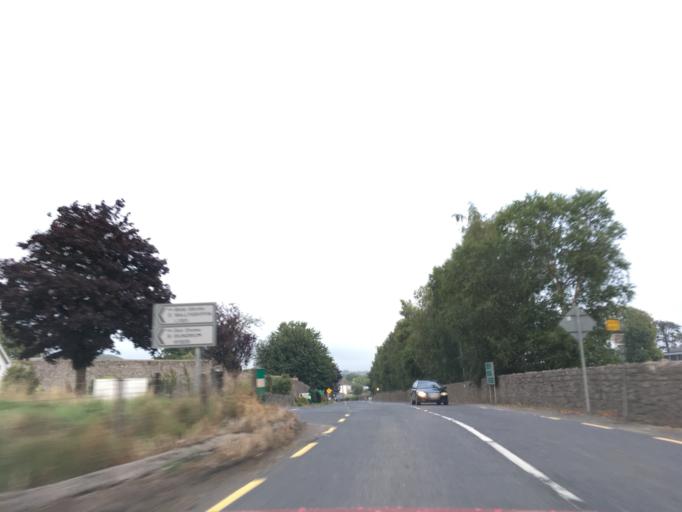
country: IE
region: Munster
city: Cashel
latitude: 52.4973
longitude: -7.9902
